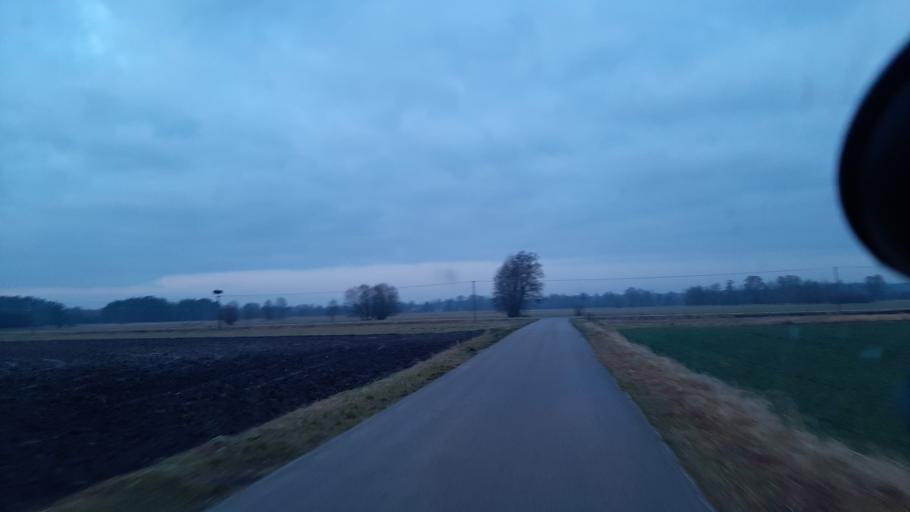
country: PL
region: Lublin Voivodeship
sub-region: Powiat lubartowski
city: Firlej
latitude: 51.5840
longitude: 22.5435
